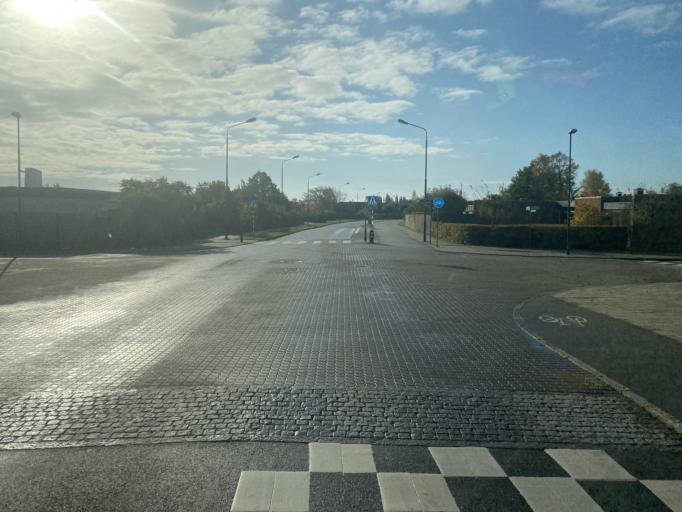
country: SE
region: Skane
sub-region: Malmo
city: Bunkeflostrand
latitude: 55.5761
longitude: 12.9637
